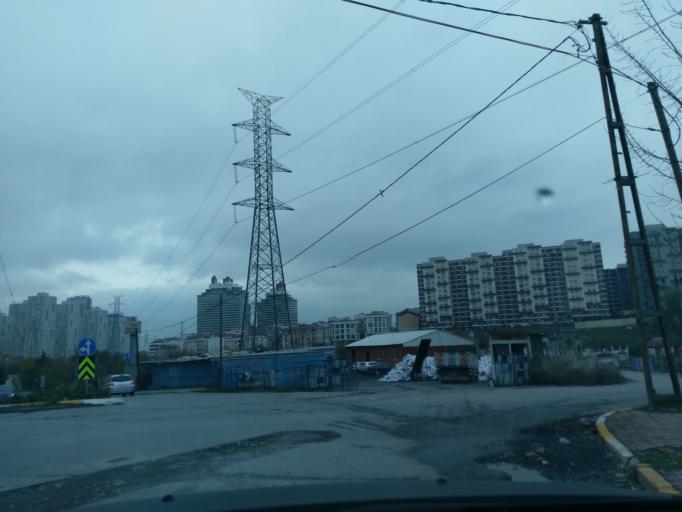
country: TR
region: Istanbul
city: Esenyurt
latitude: 41.0164
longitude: 28.6727
